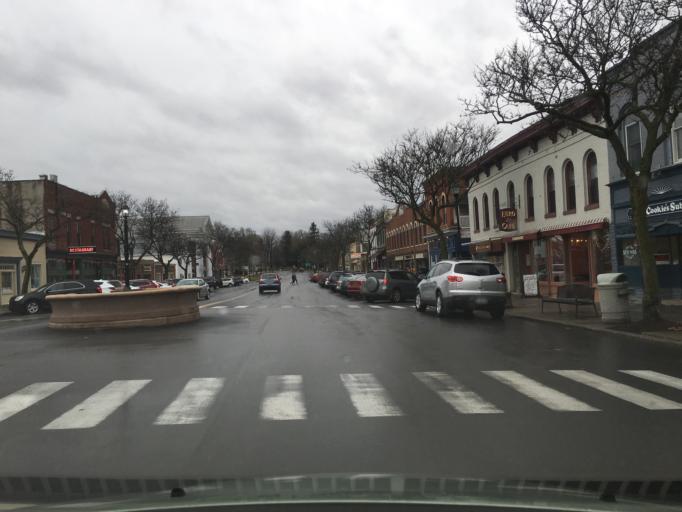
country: US
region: New York
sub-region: Livingston County
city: Geneseo
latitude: 42.7964
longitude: -77.8168
